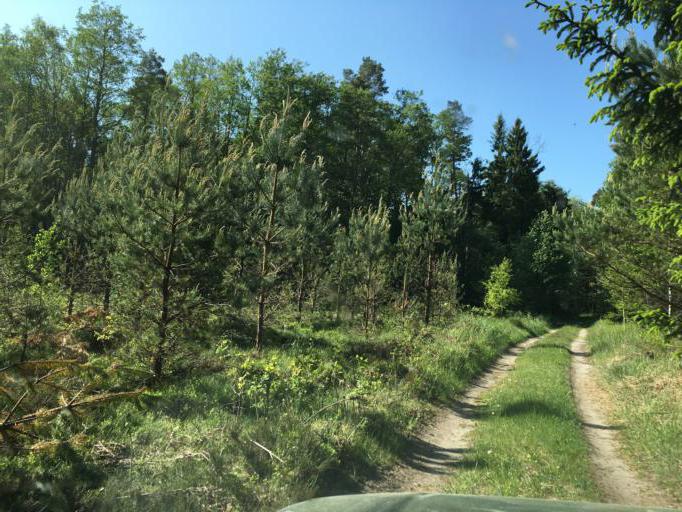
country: LV
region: Ventspils
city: Ventspils
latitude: 57.4741
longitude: 21.7655
